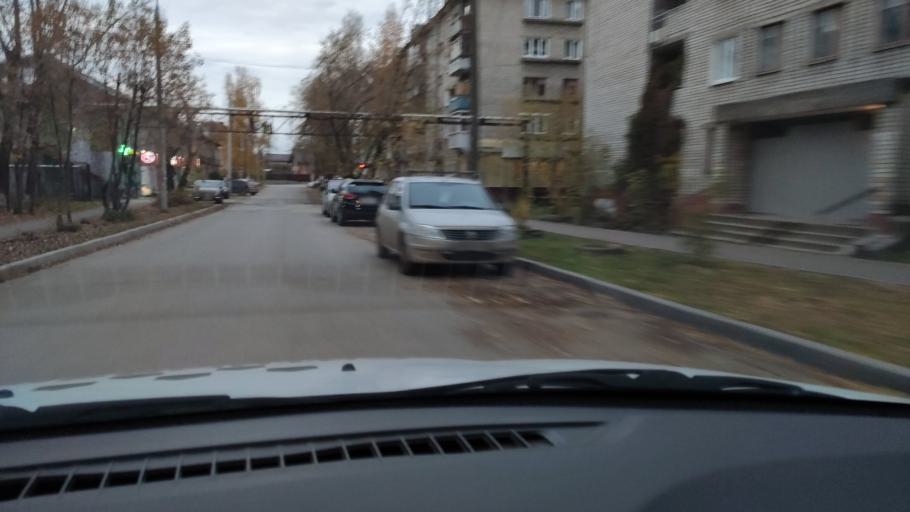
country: RU
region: Perm
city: Kondratovo
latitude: 58.0400
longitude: 56.1098
